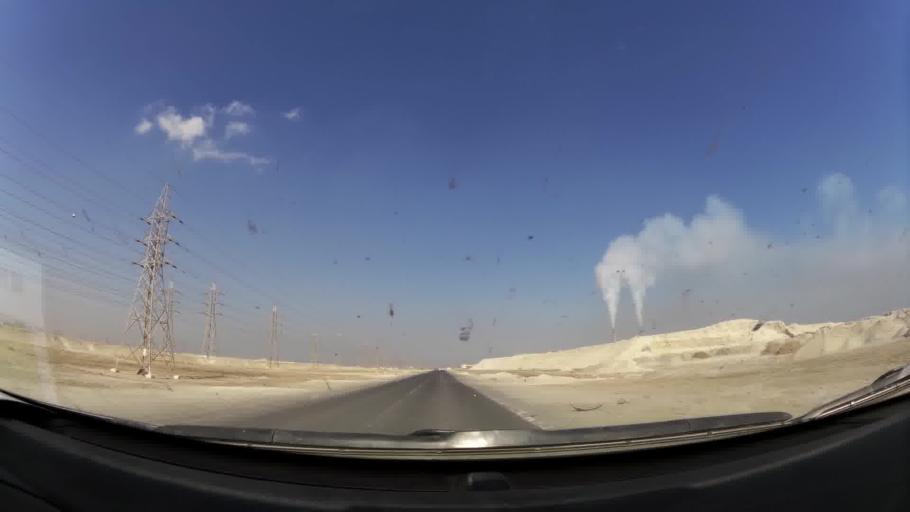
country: SA
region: Eastern Province
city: Al Khafji
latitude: 28.6877
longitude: 48.3556
